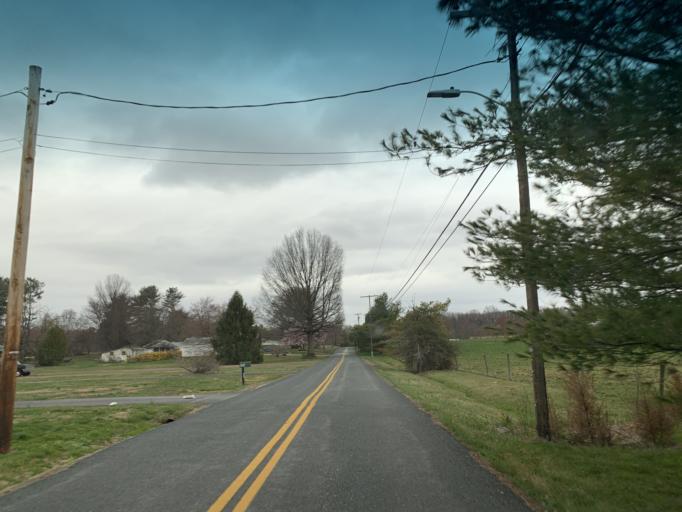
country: US
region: Maryland
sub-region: Harford County
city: Aberdeen
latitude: 39.5730
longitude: -76.1975
